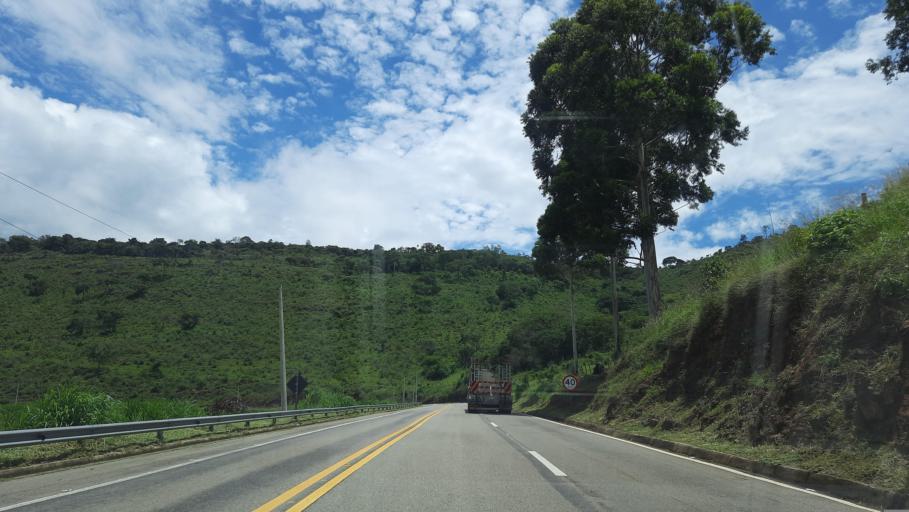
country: BR
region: Sao Paulo
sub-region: Vargem Grande Do Sul
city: Vargem Grande do Sul
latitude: -21.8302
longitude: -46.7660
